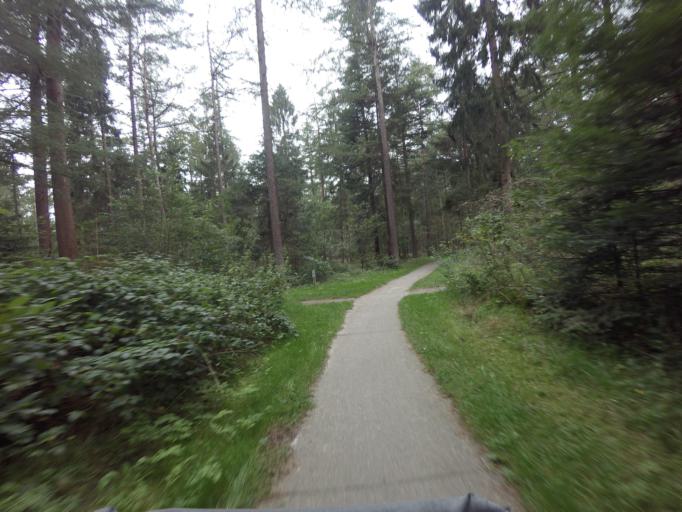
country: NL
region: Overijssel
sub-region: Gemeente Steenwijkerland
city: Tuk
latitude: 52.8235
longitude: 6.1024
